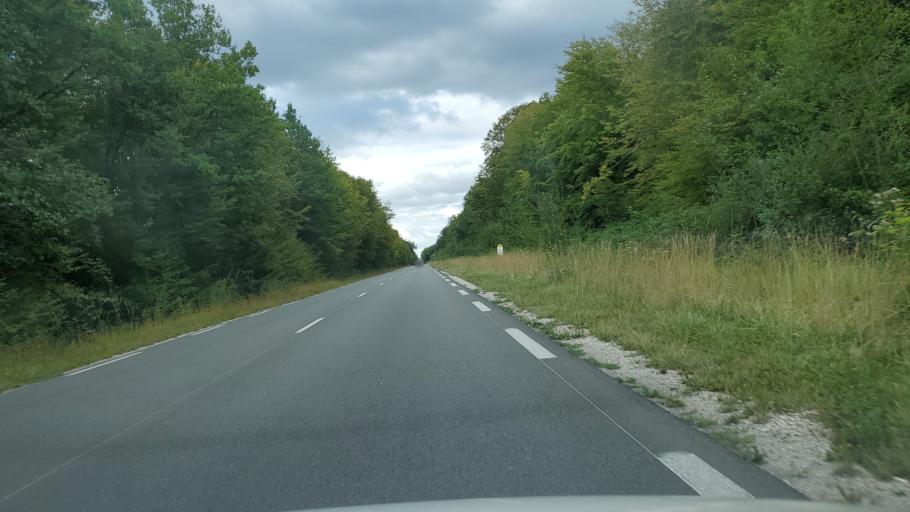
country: FR
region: Ile-de-France
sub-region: Departement de Seine-et-Marne
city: Mortcerf
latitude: 48.7721
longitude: 2.9065
